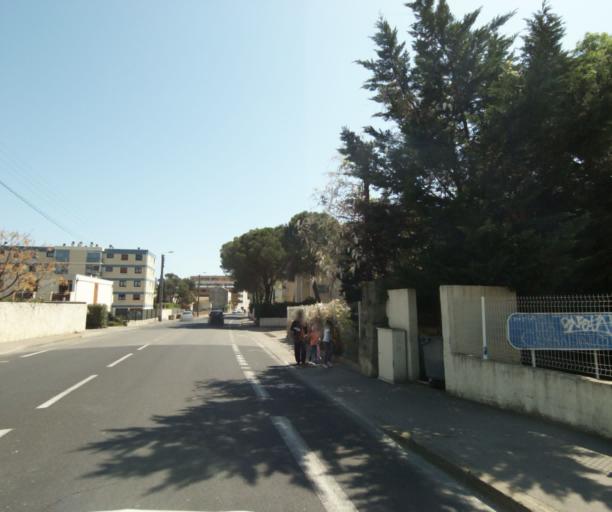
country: FR
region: Languedoc-Roussillon
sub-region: Departement de l'Herault
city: Montpellier
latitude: 43.6245
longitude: 3.8525
